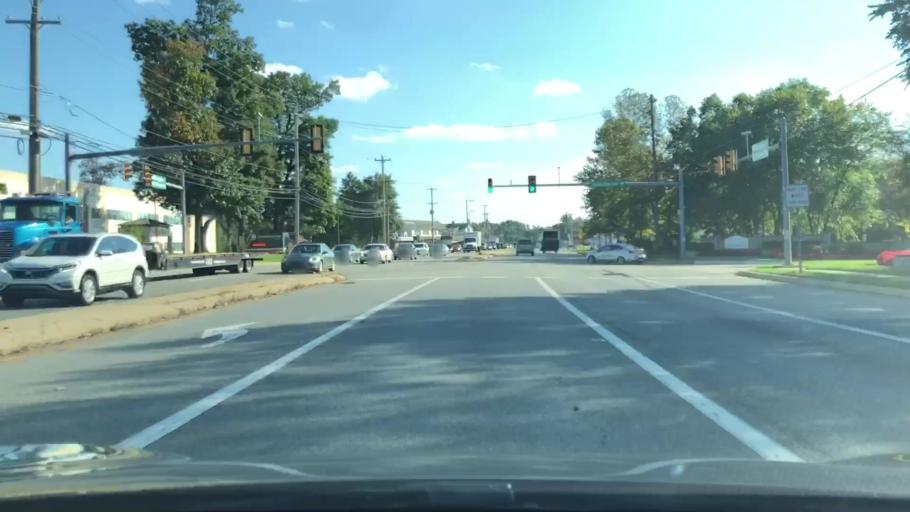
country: US
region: Pennsylvania
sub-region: Delaware County
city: Chester Heights
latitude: 39.8478
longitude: -75.5378
